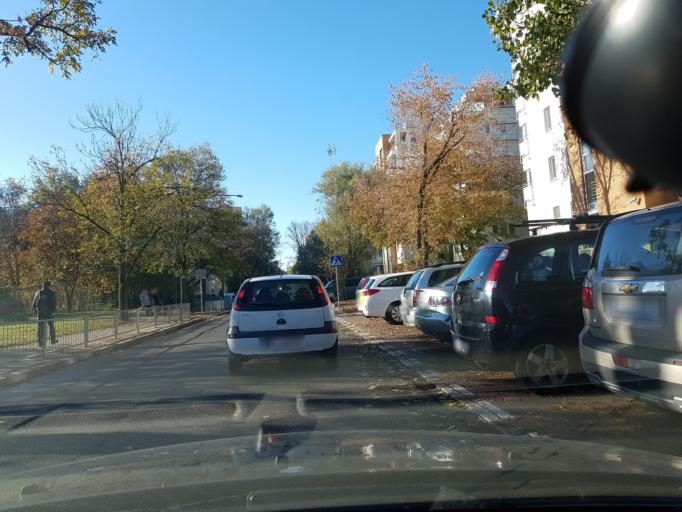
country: PL
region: Masovian Voivodeship
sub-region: Warszawa
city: Bielany
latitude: 52.2837
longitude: 20.9381
